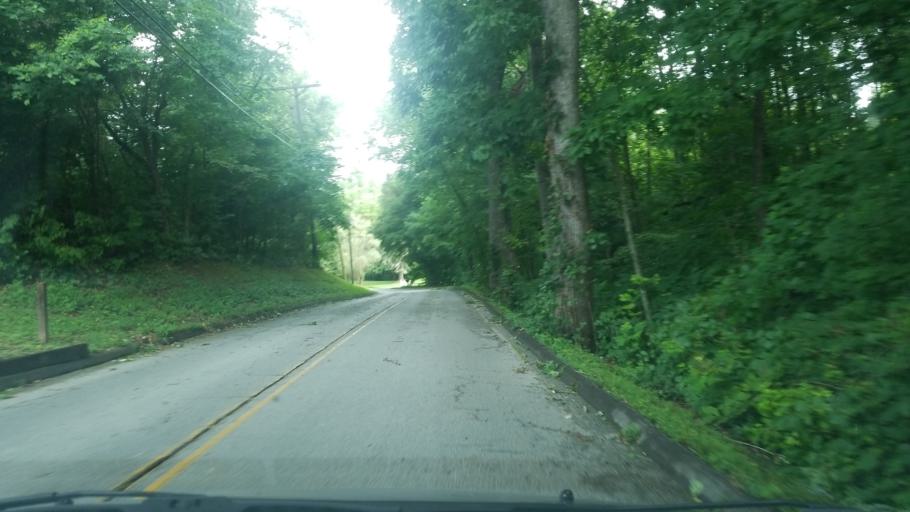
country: US
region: Tennessee
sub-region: Hamilton County
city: Apison
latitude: 35.0264
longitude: -85.0479
